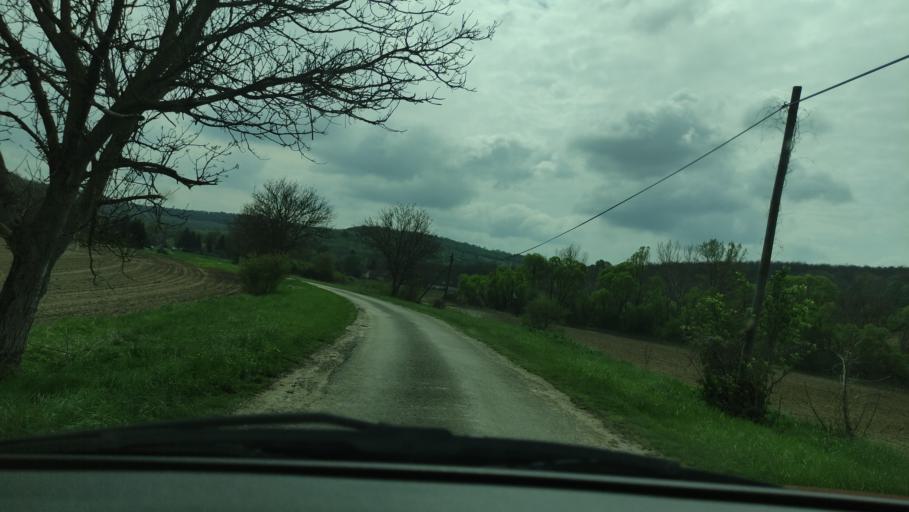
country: HU
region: Baranya
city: Sasd
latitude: 46.2839
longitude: 18.1362
